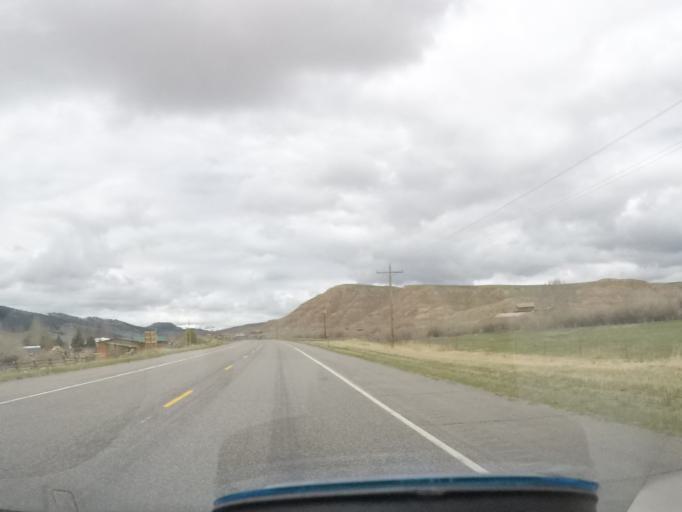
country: US
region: Wyoming
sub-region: Sublette County
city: Pinedale
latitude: 43.5659
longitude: -109.7053
